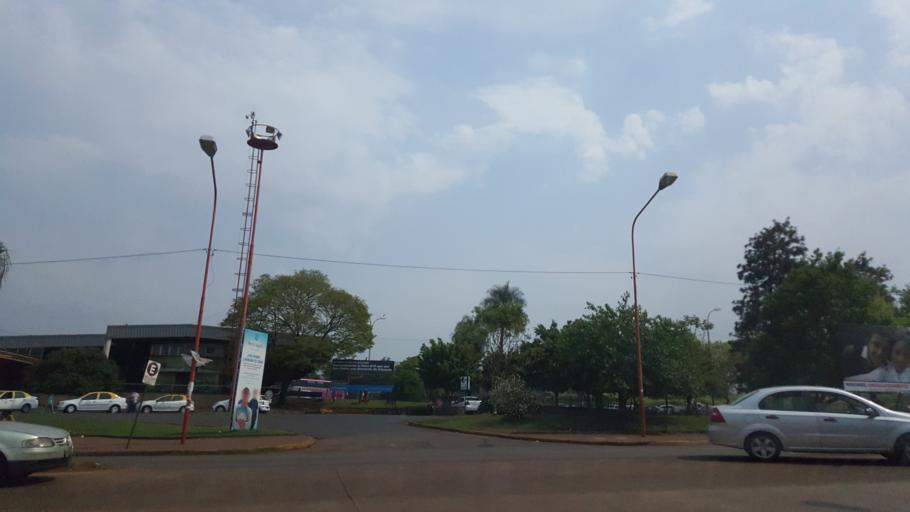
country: AR
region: Misiones
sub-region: Departamento de Capital
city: Posadas
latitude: -27.4016
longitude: -55.9135
